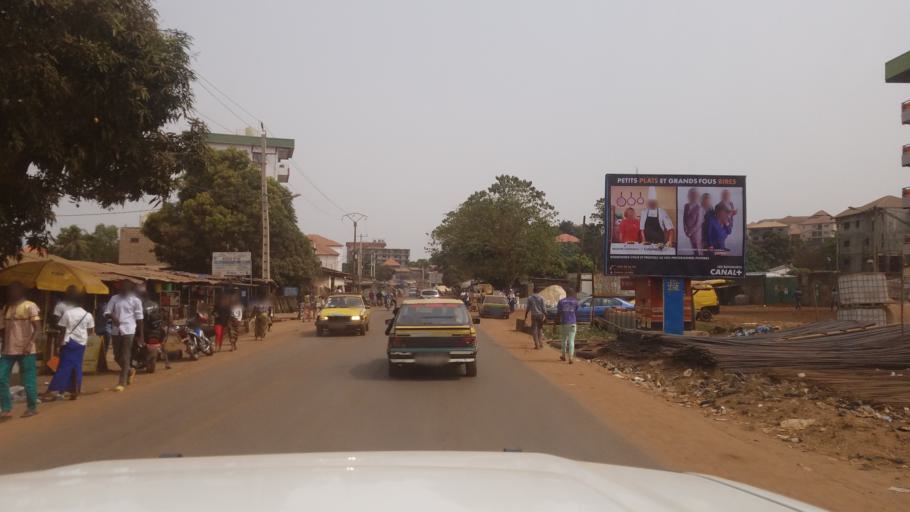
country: GN
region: Conakry
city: Conakry
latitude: 9.6540
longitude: -13.6011
